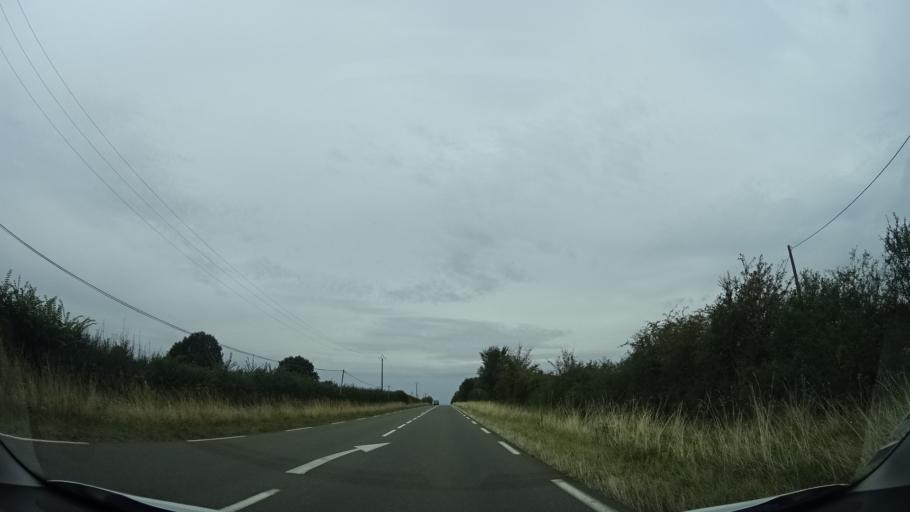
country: FR
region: Pays de la Loire
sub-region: Departement de la Sarthe
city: Auvers-le-Hamon
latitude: 47.9051
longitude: -0.4471
